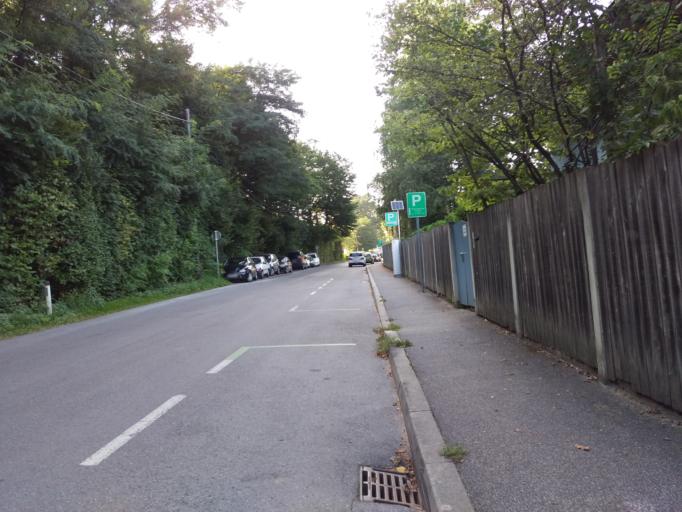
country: AT
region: Styria
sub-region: Graz Stadt
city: Graz
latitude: 47.0860
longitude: 15.4521
